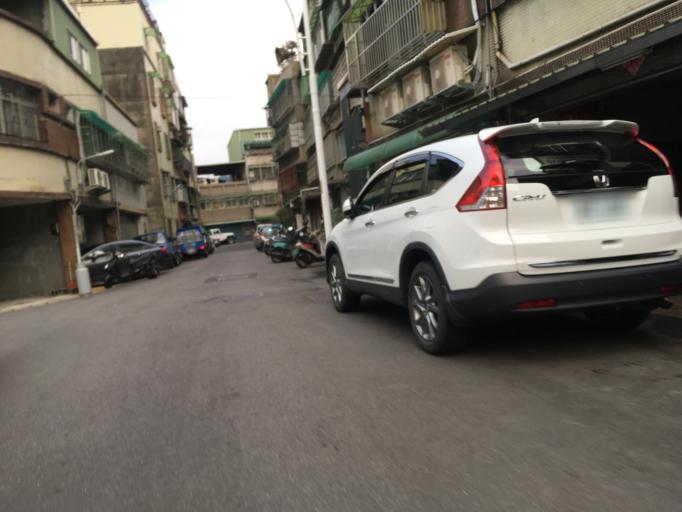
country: TW
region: Taiwan
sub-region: Taoyuan
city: Taoyuan
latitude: 24.9300
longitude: 121.3681
